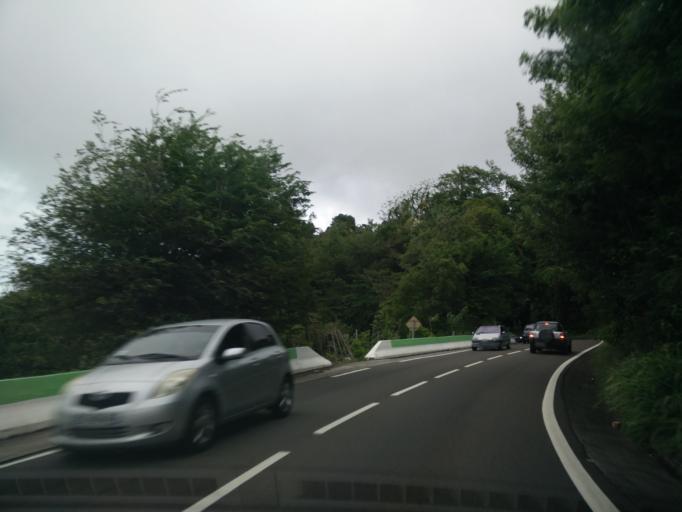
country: MQ
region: Martinique
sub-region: Martinique
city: Le Marin
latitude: 14.4942
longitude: -60.8594
